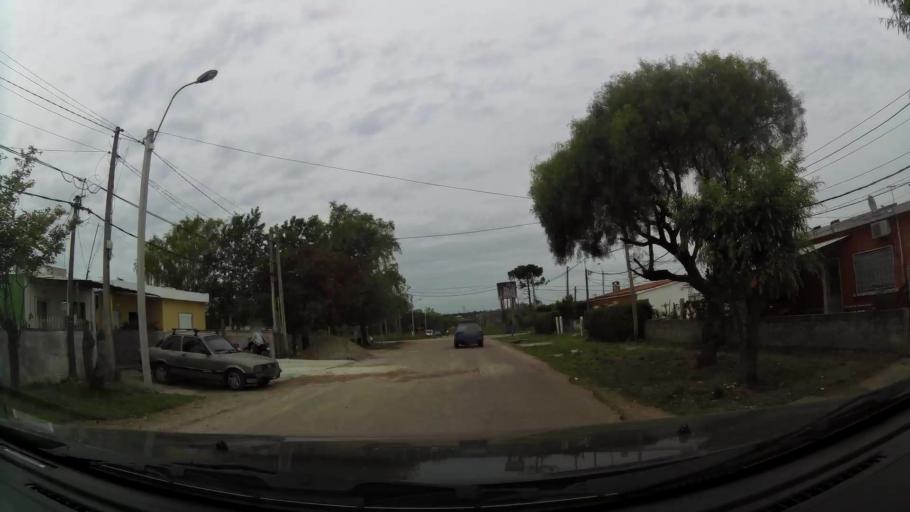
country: UY
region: Canelones
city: Las Piedras
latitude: -34.7190
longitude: -56.1921
